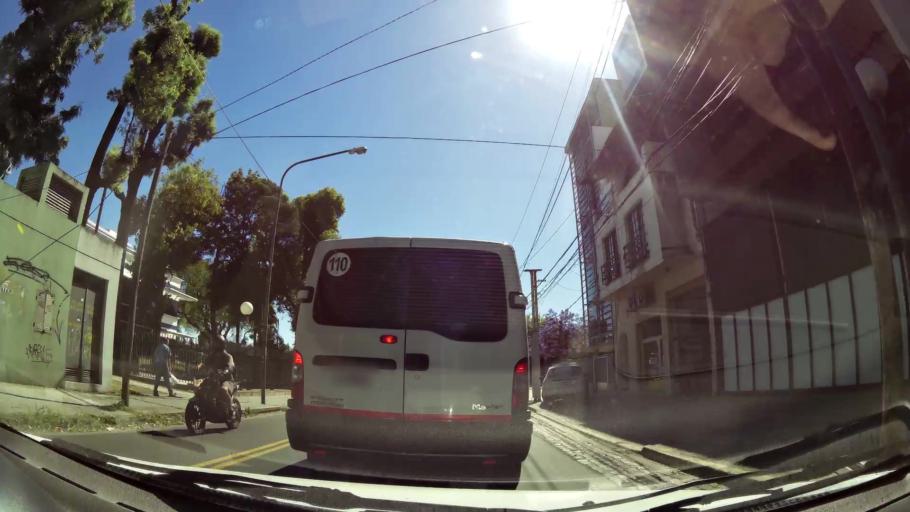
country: AR
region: Buenos Aires
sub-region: Partido de Vicente Lopez
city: Olivos
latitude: -34.5247
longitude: -58.5131
